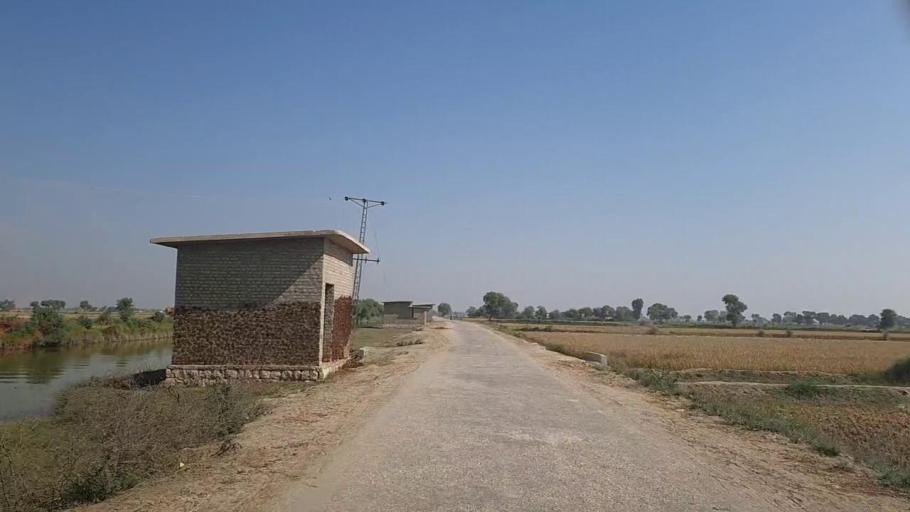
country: PK
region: Sindh
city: Thul
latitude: 28.2493
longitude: 68.8111
